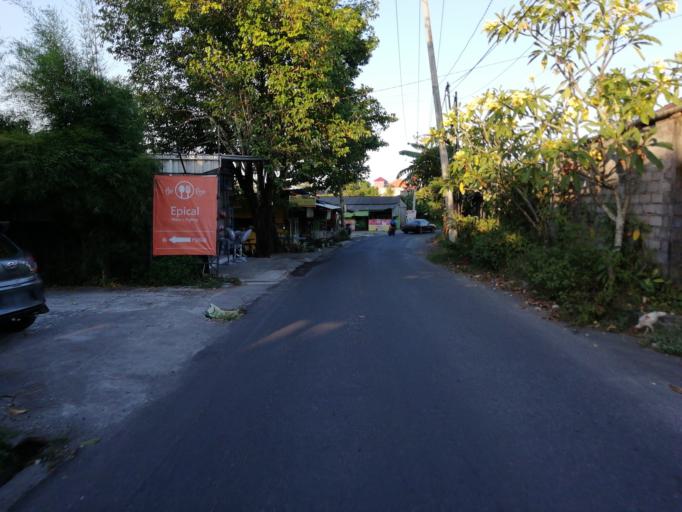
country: ID
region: Bali
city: Bualu
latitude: -8.8075
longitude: 115.1964
